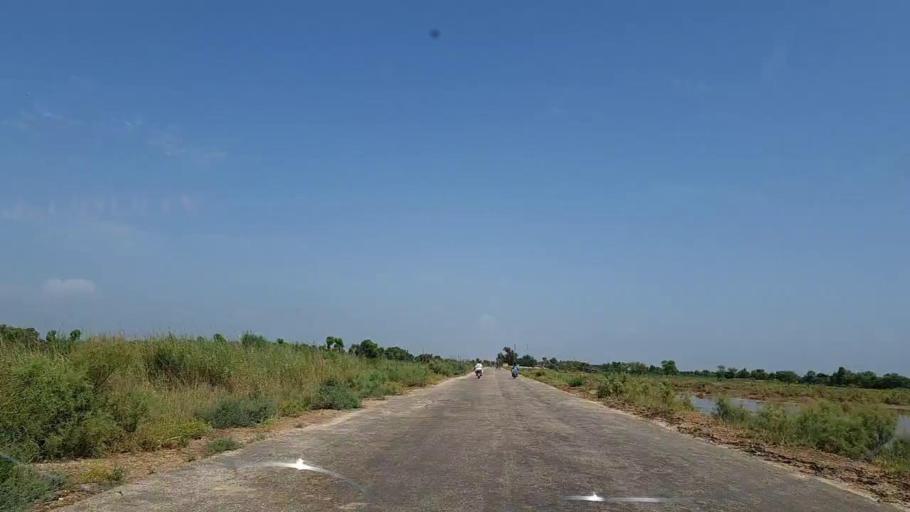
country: PK
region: Sindh
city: Naushahro Firoz
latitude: 26.8153
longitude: 68.1838
